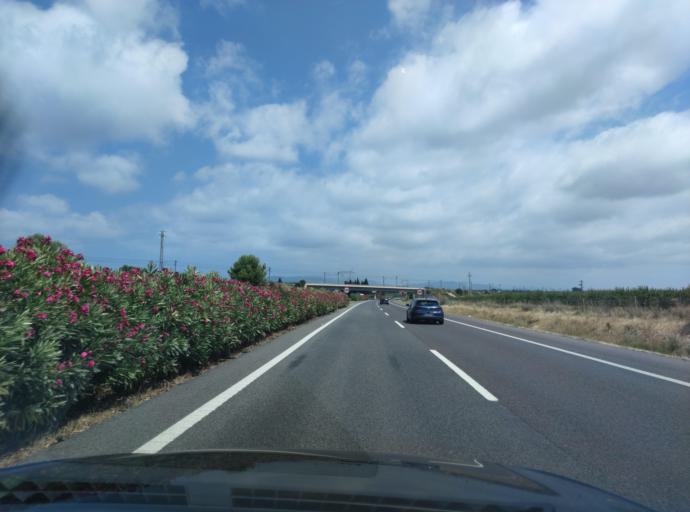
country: ES
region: Catalonia
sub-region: Provincia de Tarragona
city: Amposta
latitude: 40.7401
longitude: 0.5916
